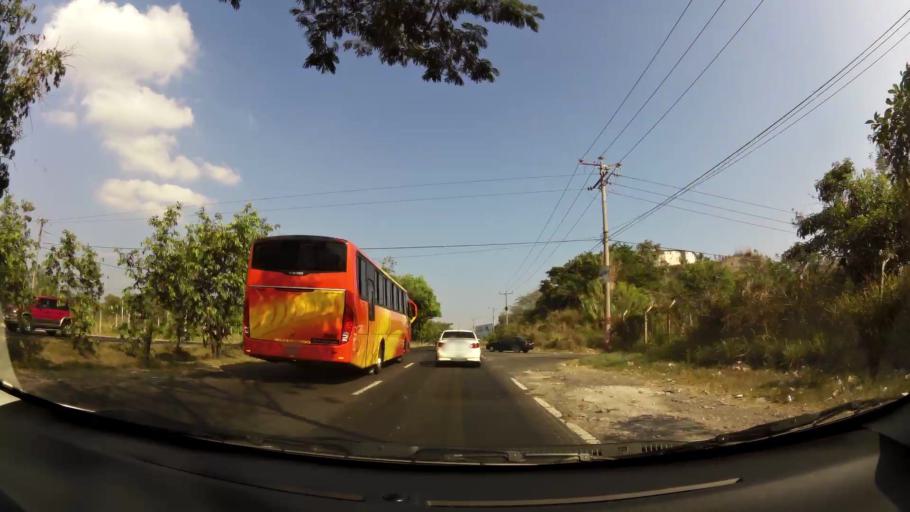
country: SV
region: San Salvador
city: Ilopango
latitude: 13.7112
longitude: -89.1134
